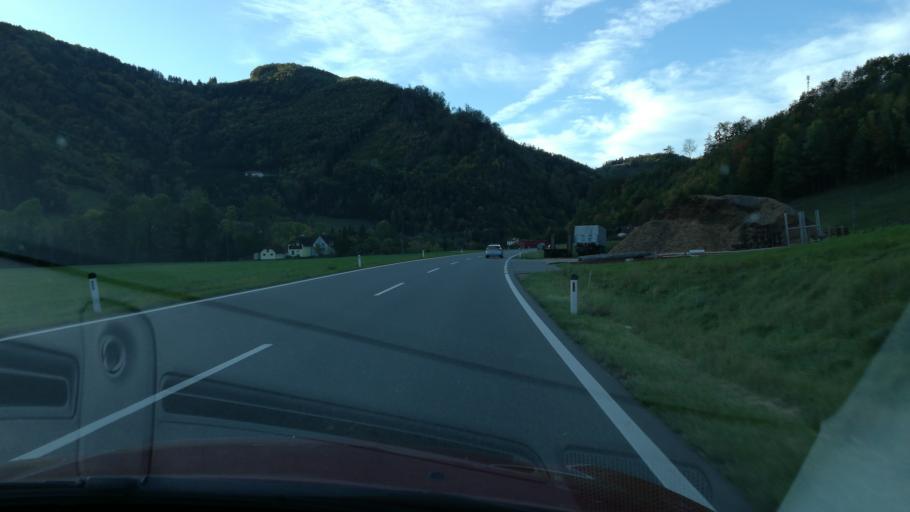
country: AT
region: Upper Austria
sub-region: Politischer Bezirk Steyr-Land
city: Ternberg
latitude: 47.9328
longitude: 14.3595
